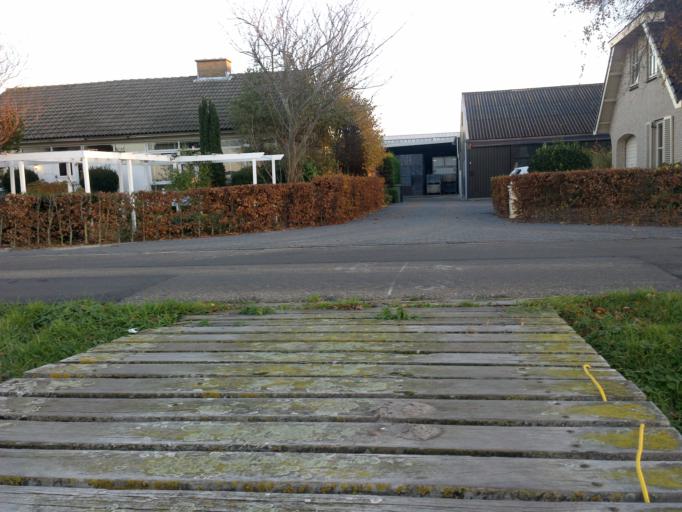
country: NL
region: South Holland
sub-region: Gemeente Teylingen
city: Sassenheim
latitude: 52.2345
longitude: 4.5071
